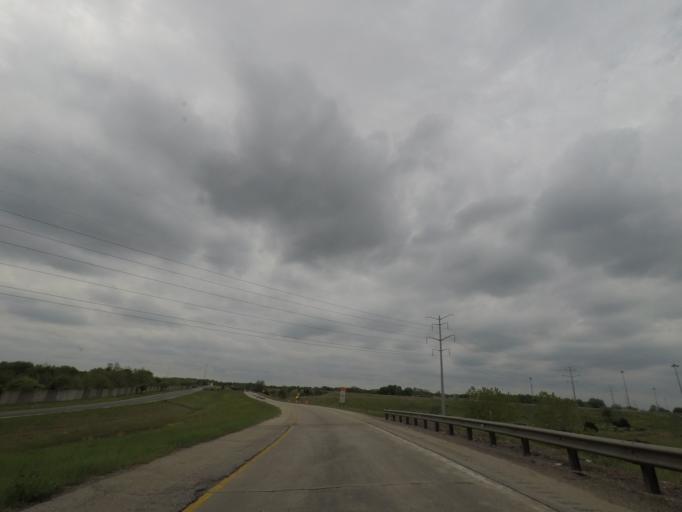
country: US
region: Illinois
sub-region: Winnebago County
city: Cherry Valley
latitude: 42.2201
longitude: -89.0071
